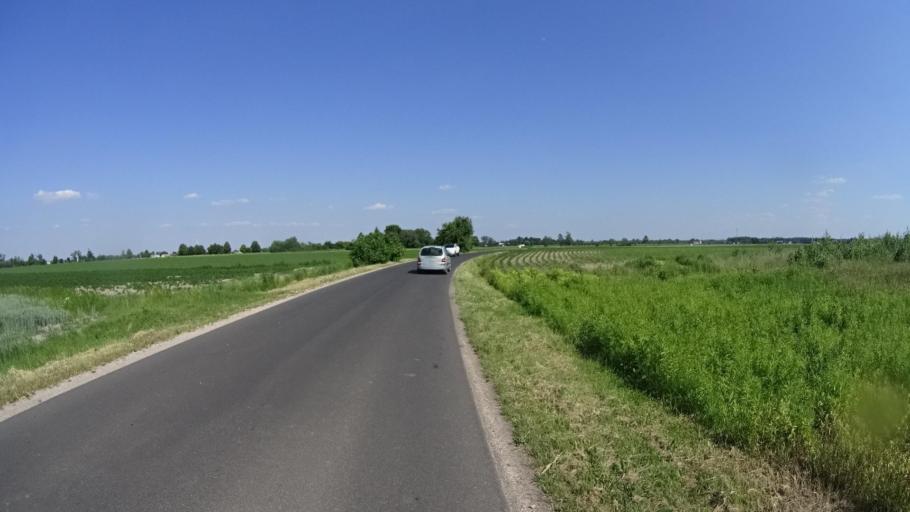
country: PL
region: Masovian Voivodeship
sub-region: Powiat warszawski zachodni
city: Blonie
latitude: 52.1628
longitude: 20.6496
